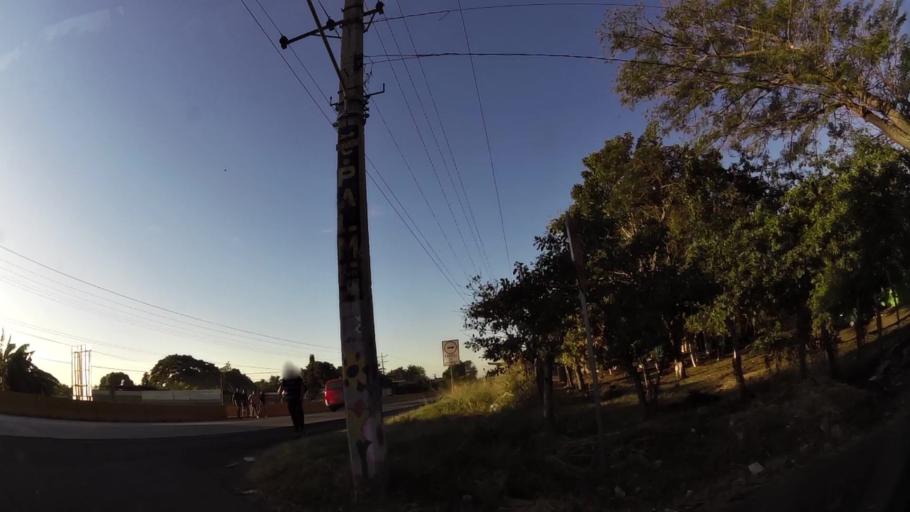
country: SV
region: Sonsonate
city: San Antonio del Monte
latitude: 13.7059
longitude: -89.7310
